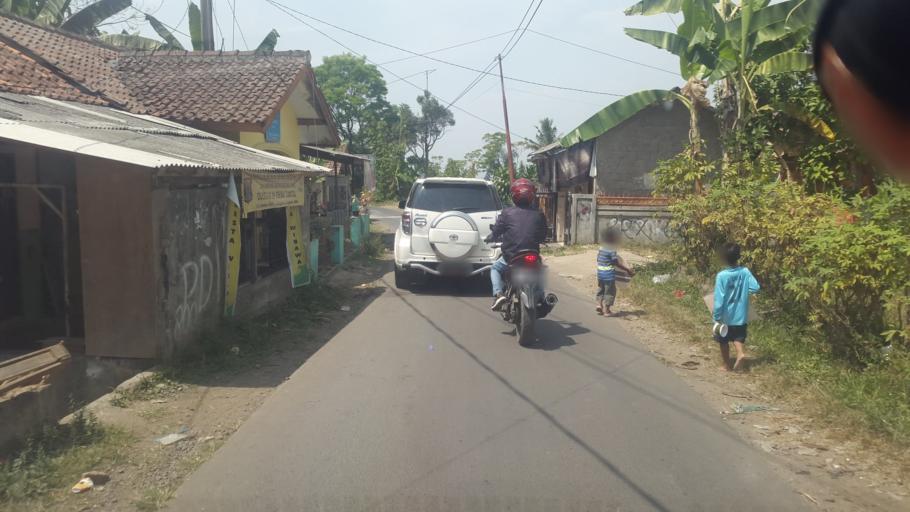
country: ID
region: West Java
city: Cicurug
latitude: -6.7773
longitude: 106.7404
